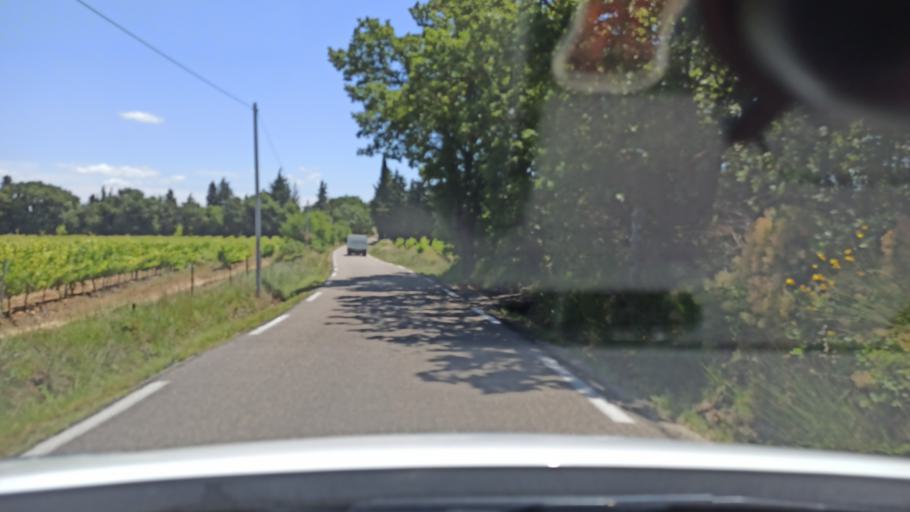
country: FR
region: Provence-Alpes-Cote d'Azur
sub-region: Departement du Vaucluse
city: Caumont-sur-Durance
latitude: 43.9035
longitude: 4.9295
